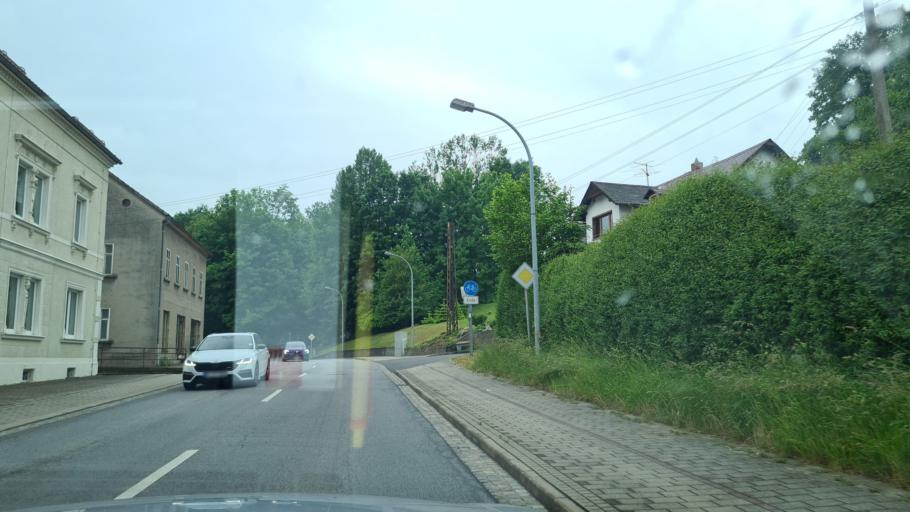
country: DE
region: Saxony
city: Schirgiswalde
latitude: 51.0718
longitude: 14.4289
